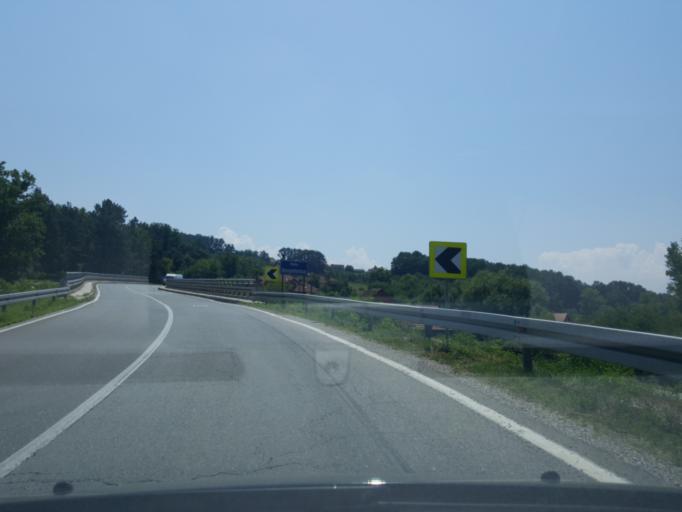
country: RS
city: Prislonica
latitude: 43.9700
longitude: 20.4178
